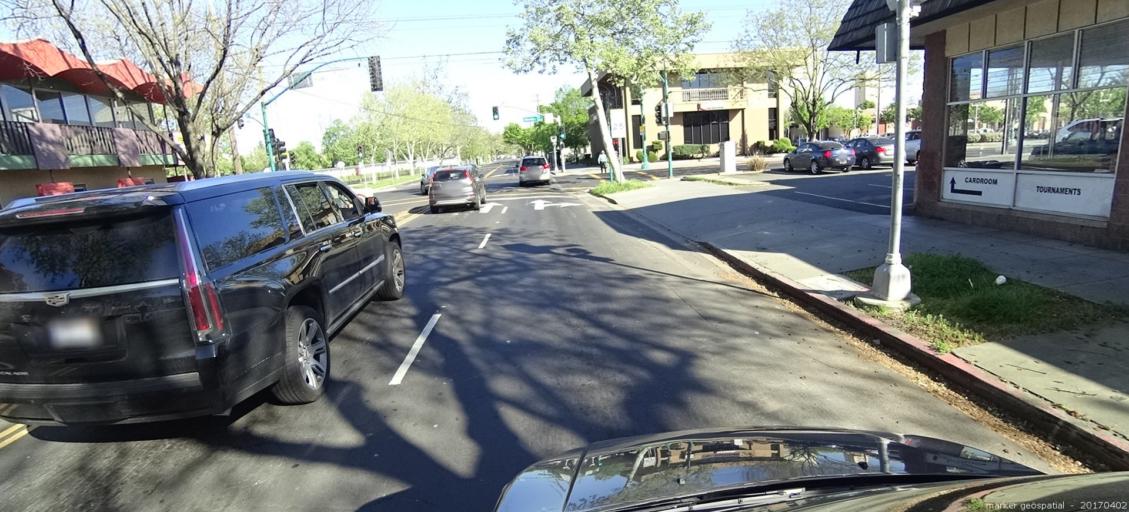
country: US
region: California
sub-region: Sacramento County
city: Sacramento
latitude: 38.5729
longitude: -121.4658
